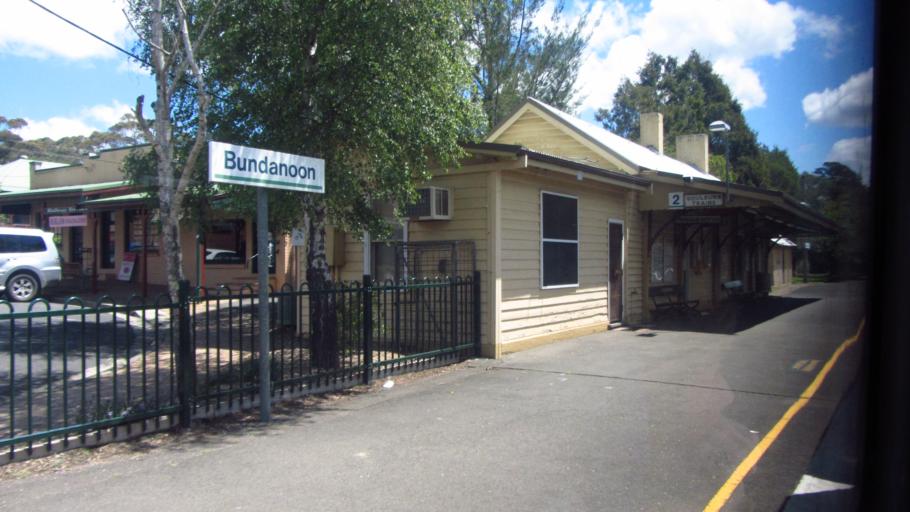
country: AU
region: New South Wales
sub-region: Wingecarribee
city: Bundanoon
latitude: -34.6558
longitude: 150.3004
